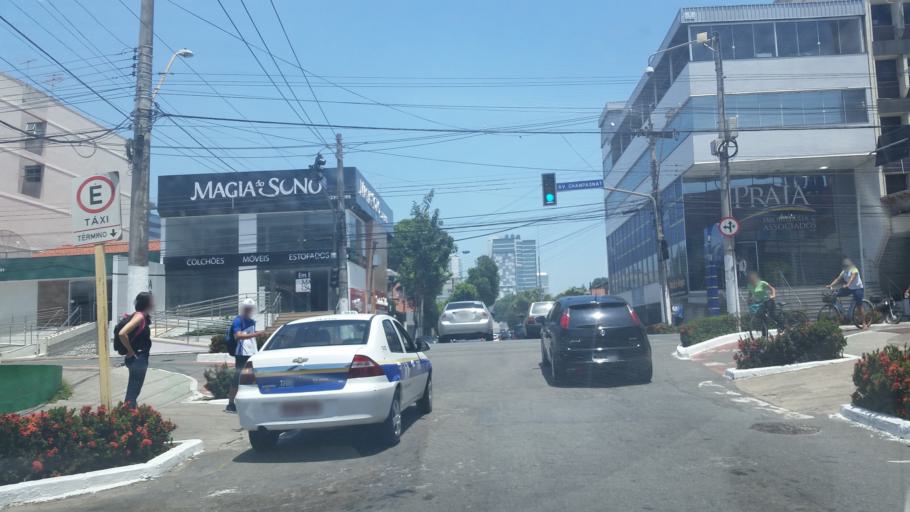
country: BR
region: Espirito Santo
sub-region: Vila Velha
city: Vila Velha
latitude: -20.3363
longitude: -40.2882
